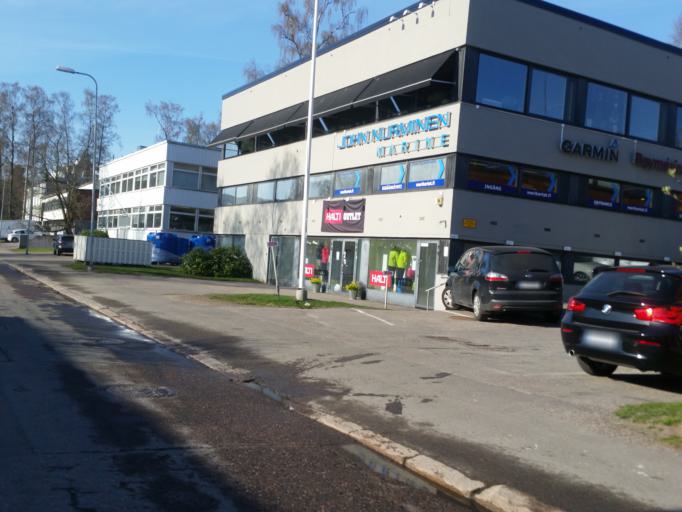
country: FI
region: Uusimaa
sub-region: Helsinki
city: Helsinki
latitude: 60.1508
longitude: 24.8878
